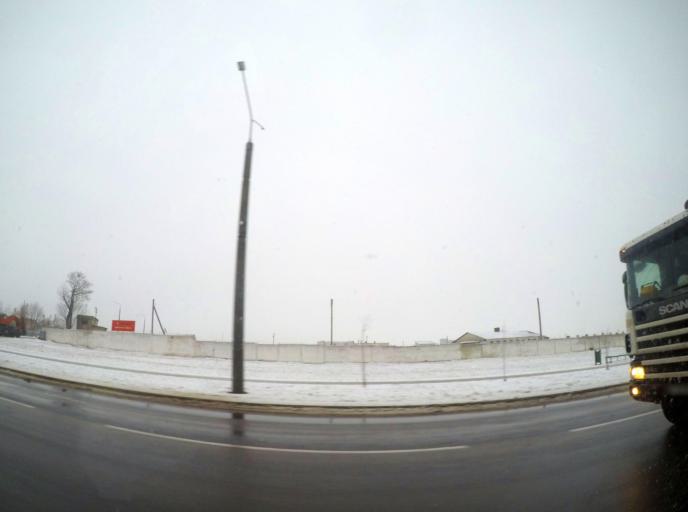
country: BY
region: Grodnenskaya
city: Hrodna
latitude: 53.6386
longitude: 23.8143
